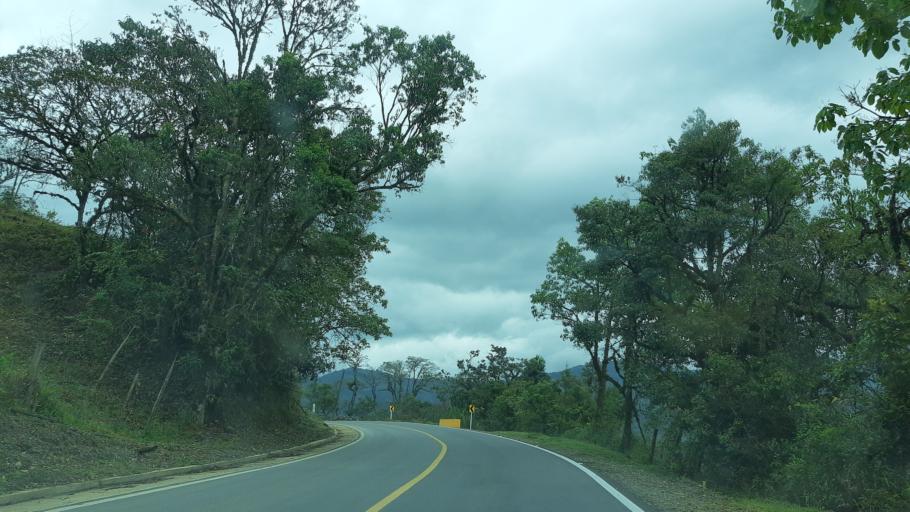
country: CO
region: Boyaca
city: Chivor
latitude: 4.9675
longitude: -73.3283
